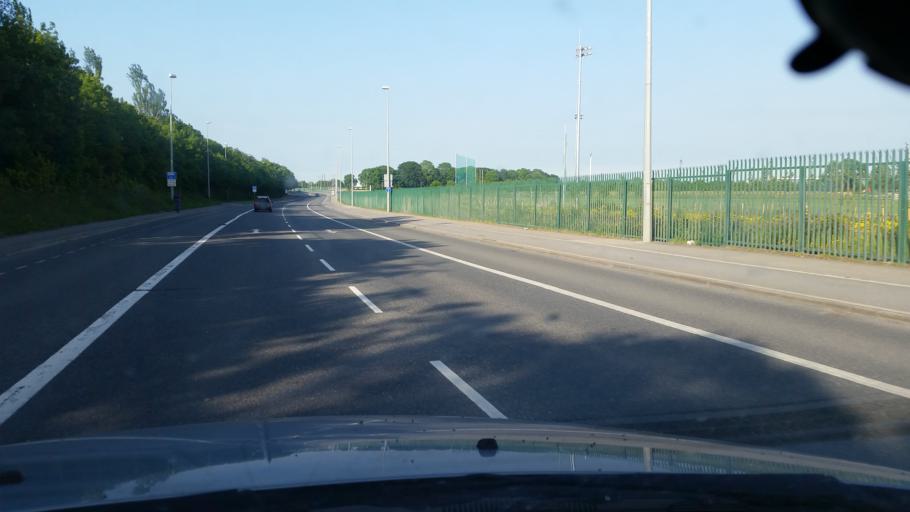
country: IE
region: Leinster
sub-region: Fingal County
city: Blanchardstown
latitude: 53.3994
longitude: -6.3684
